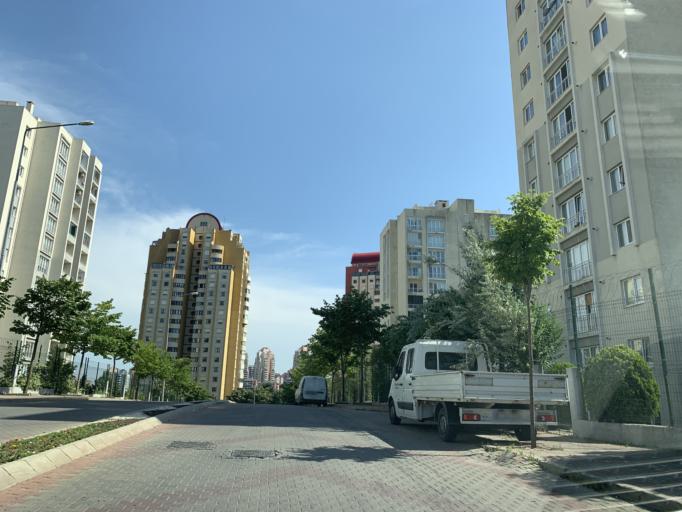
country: TR
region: Istanbul
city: Esenyurt
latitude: 41.0734
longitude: 28.6791
